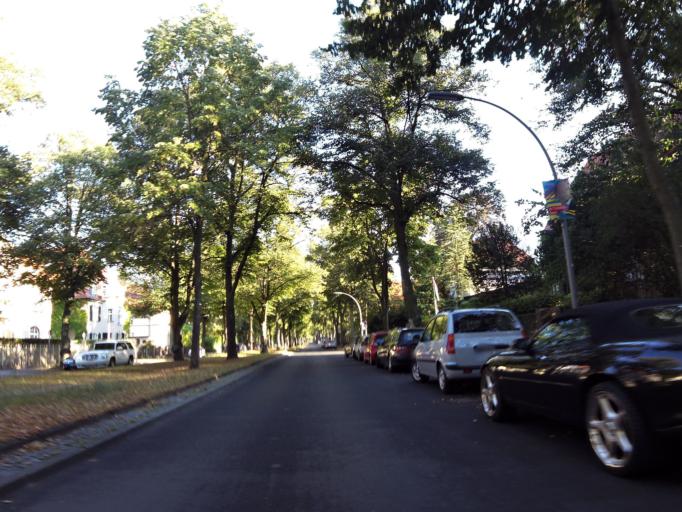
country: DE
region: Berlin
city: Dahlem
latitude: 52.4625
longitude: 13.2990
